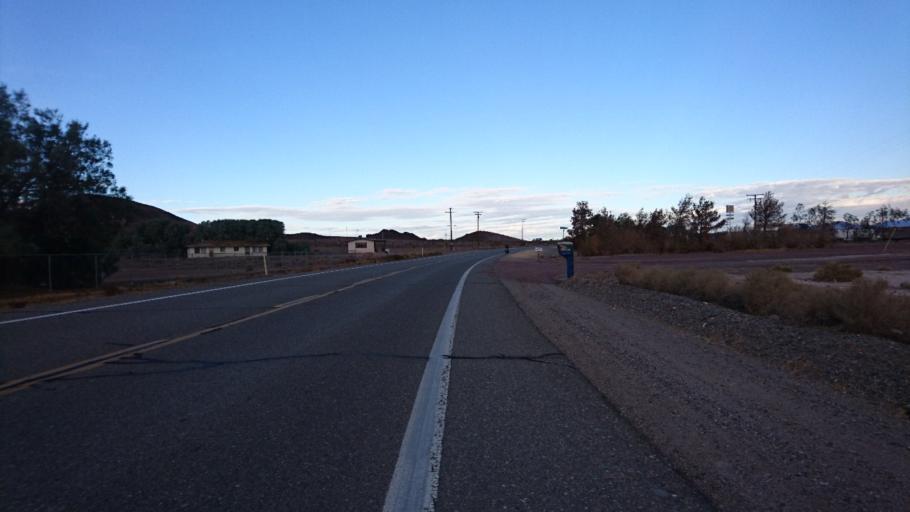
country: US
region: California
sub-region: San Bernardino County
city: Barstow
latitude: 34.8272
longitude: -116.6898
